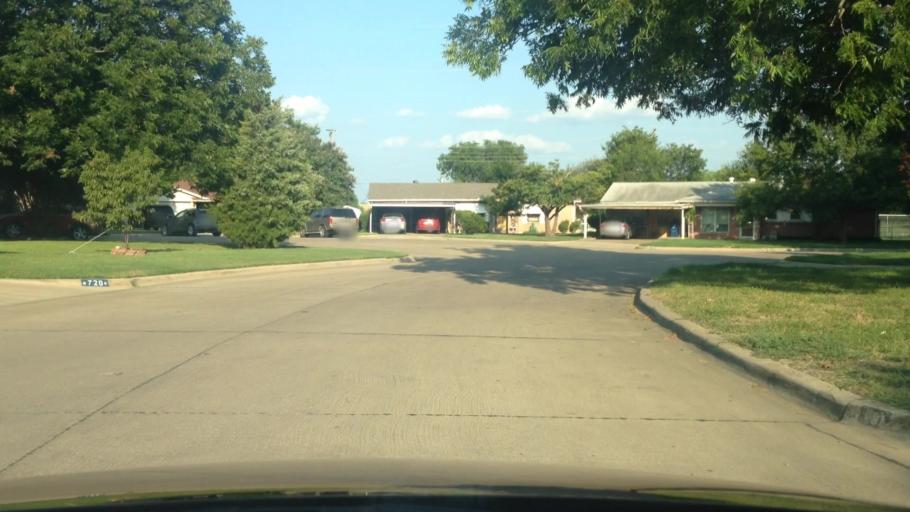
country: US
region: Texas
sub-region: Tarrant County
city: Everman
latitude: 32.6286
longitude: -97.2917
